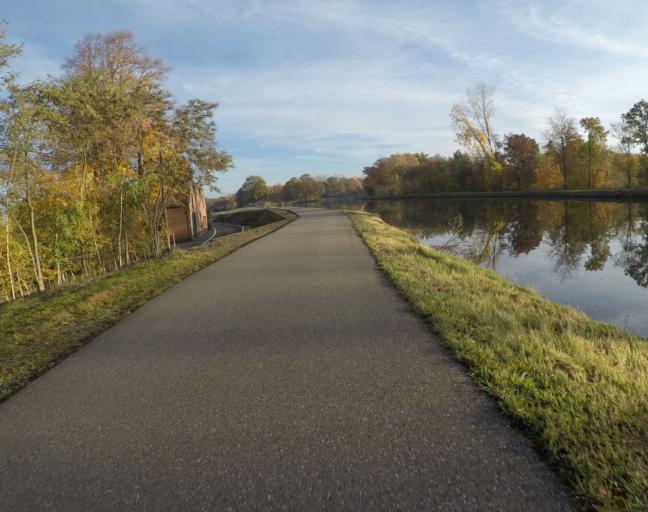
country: BE
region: Flanders
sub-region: Provincie Antwerpen
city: Geel
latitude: 51.1957
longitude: 4.9611
